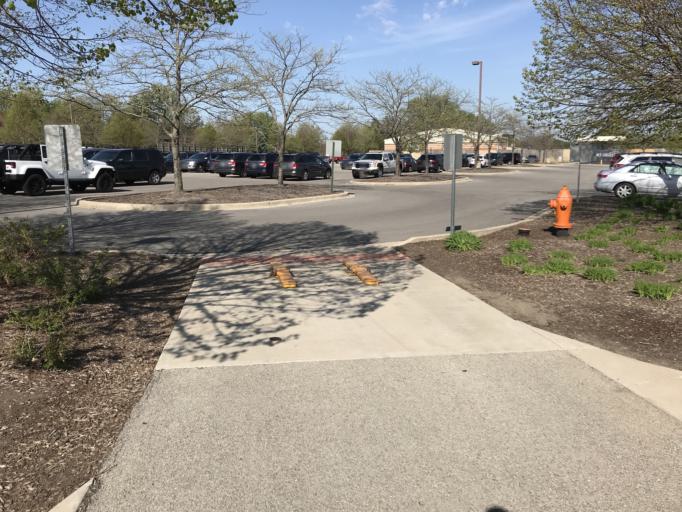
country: US
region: Illinois
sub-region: Will County
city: Plainfield
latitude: 41.7044
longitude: -88.1893
